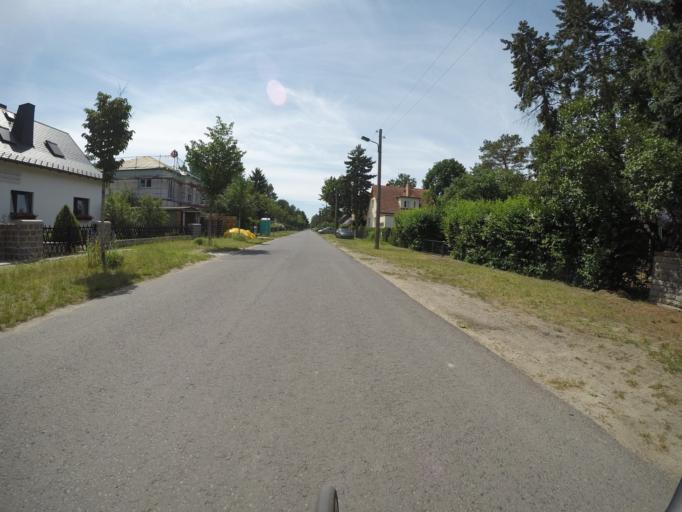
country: DE
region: Berlin
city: Mahlsdorf
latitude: 52.4817
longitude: 13.6124
